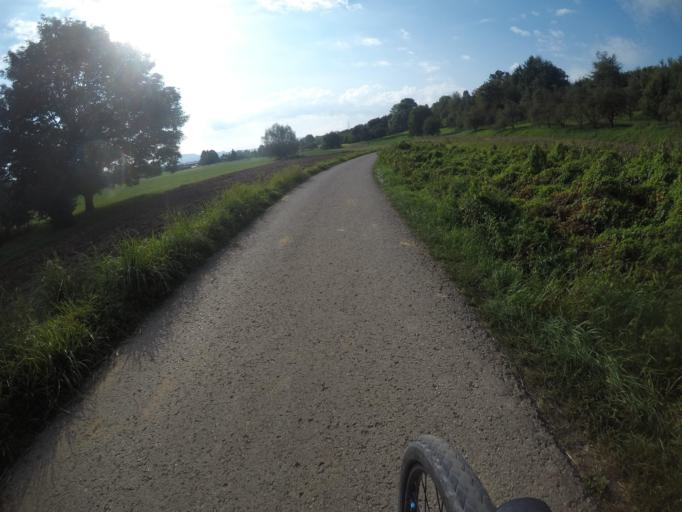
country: DE
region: Baden-Wuerttemberg
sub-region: Regierungsbezirk Stuttgart
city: Neckartenzlingen
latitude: 48.5830
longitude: 9.2437
